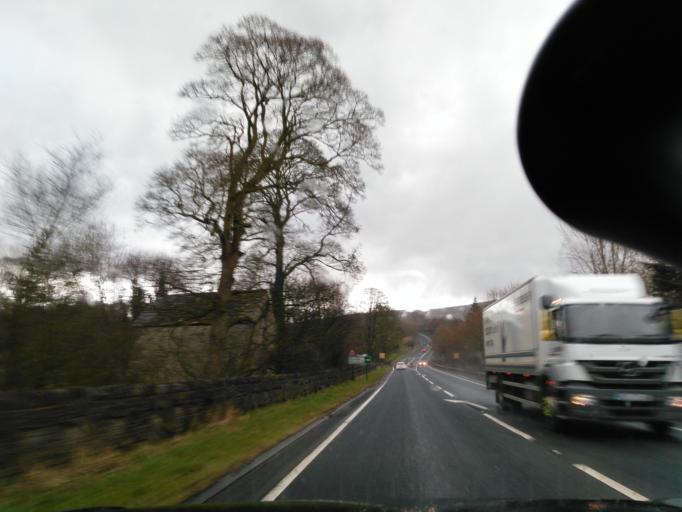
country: GB
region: England
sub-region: Bradford
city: Addingham
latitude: 53.9716
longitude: -1.8897
